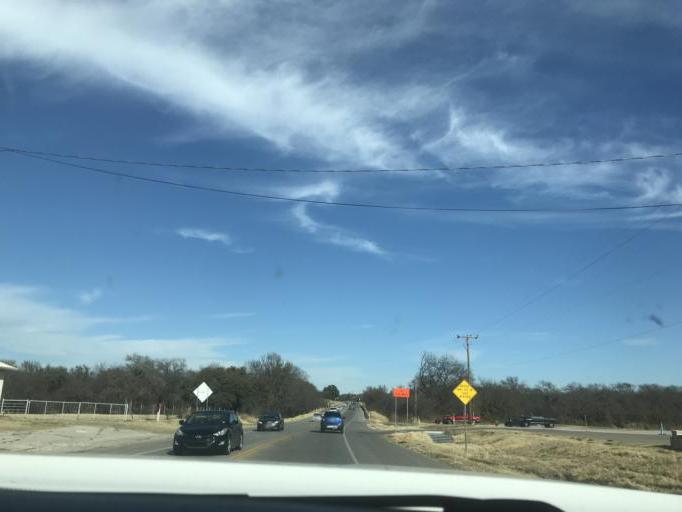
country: US
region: Texas
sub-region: Erath County
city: Stephenville
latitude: 32.2341
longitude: -98.2062
